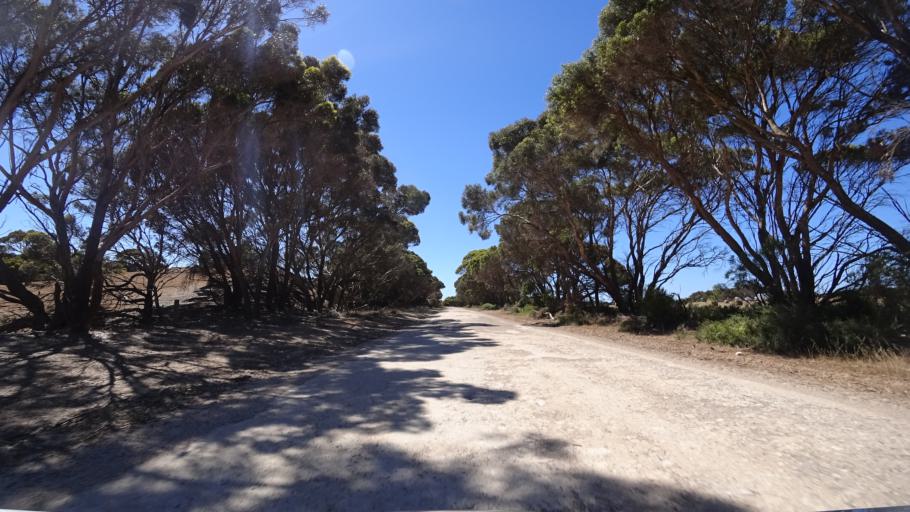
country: AU
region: South Australia
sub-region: Kangaroo Island
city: Kingscote
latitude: -35.7568
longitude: 137.7503
